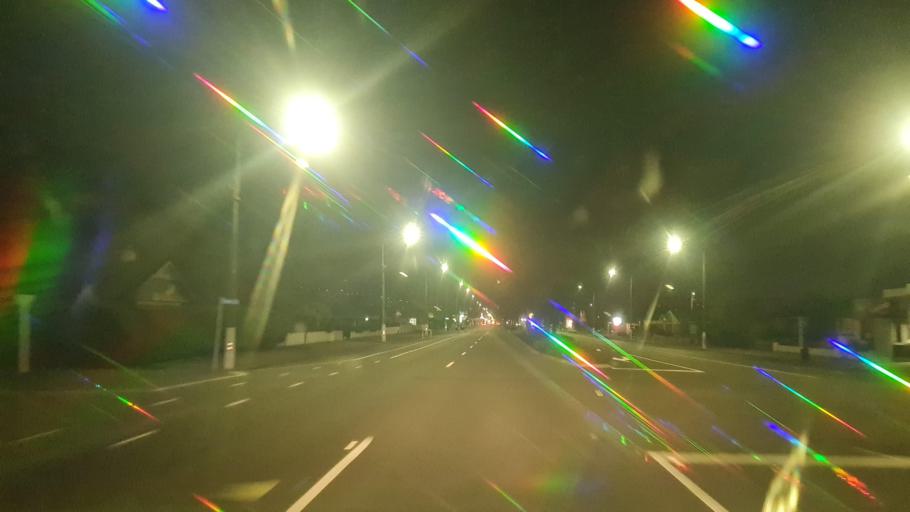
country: NZ
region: Otago
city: Oamaru
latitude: -45.0892
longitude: 170.9753
